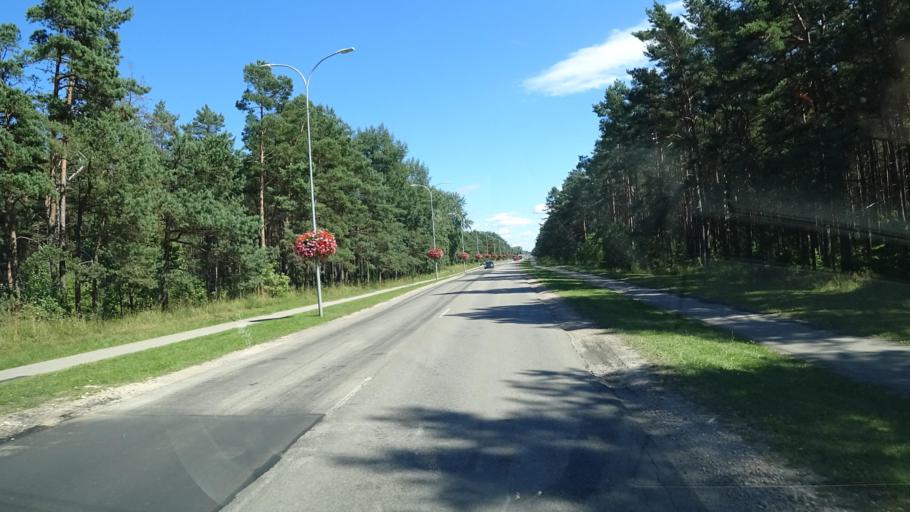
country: LV
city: Tireli
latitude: 56.9653
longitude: 23.5920
